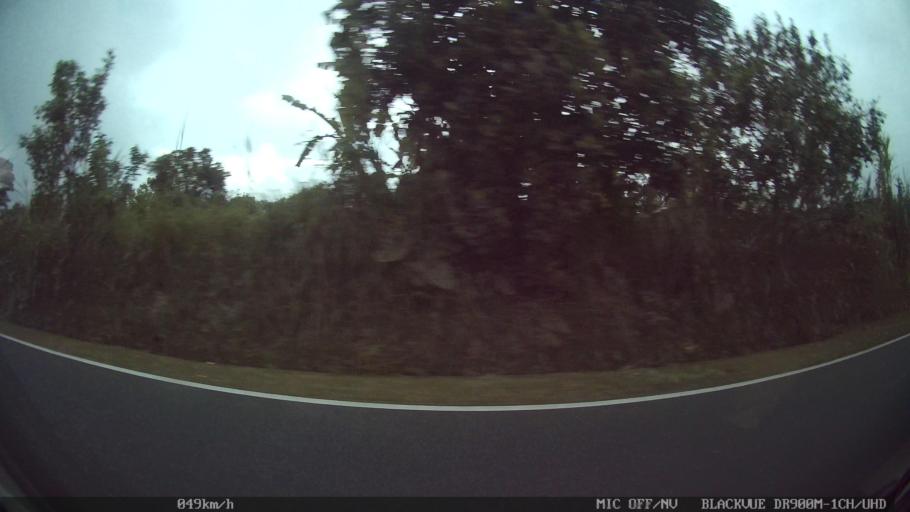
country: ID
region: Bali
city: Banjar Kedisan
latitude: -8.2775
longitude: 115.3243
